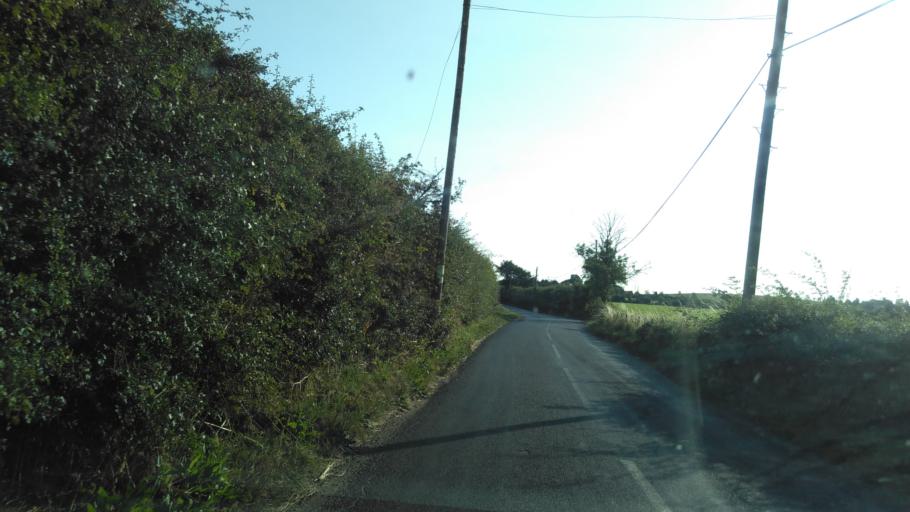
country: GB
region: England
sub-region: Kent
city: Dunkirk
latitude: 51.3218
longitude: 0.9857
